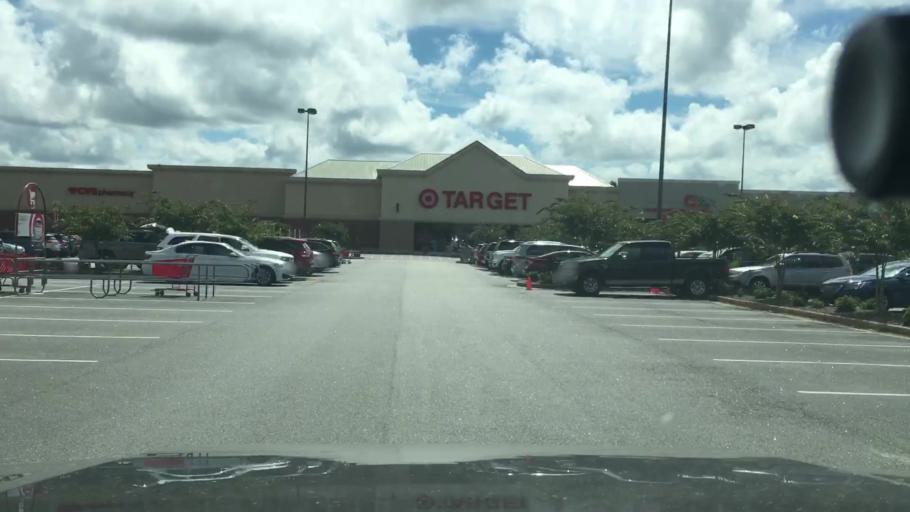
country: US
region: Georgia
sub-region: Coweta County
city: Newnan
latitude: 33.3933
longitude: -84.7598
